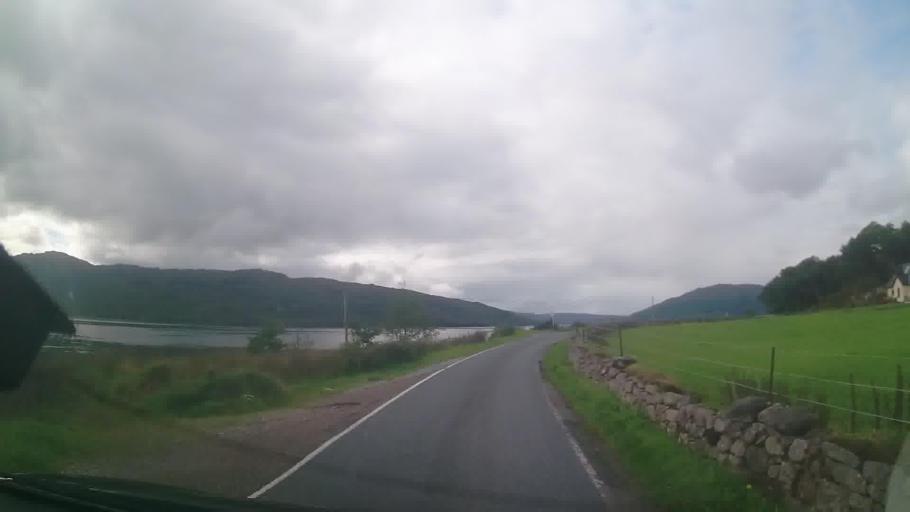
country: GB
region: Scotland
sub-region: Argyll and Bute
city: Isle Of Mull
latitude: 56.7117
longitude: -5.7239
